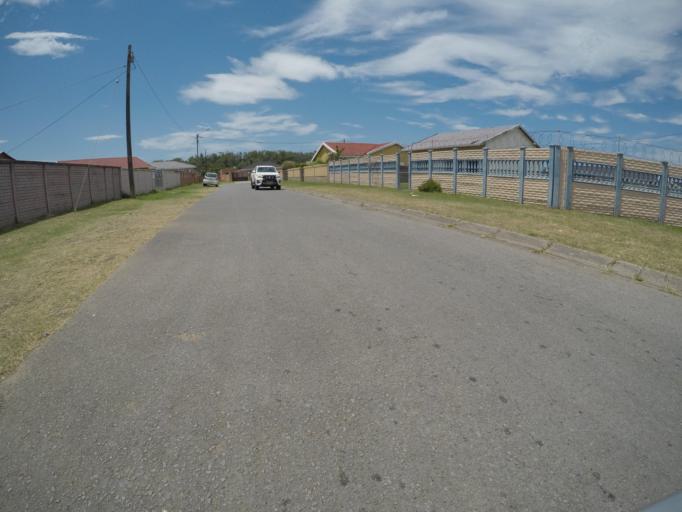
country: ZA
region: Eastern Cape
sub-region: Buffalo City Metropolitan Municipality
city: East London
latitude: -33.0463
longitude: 27.8495
